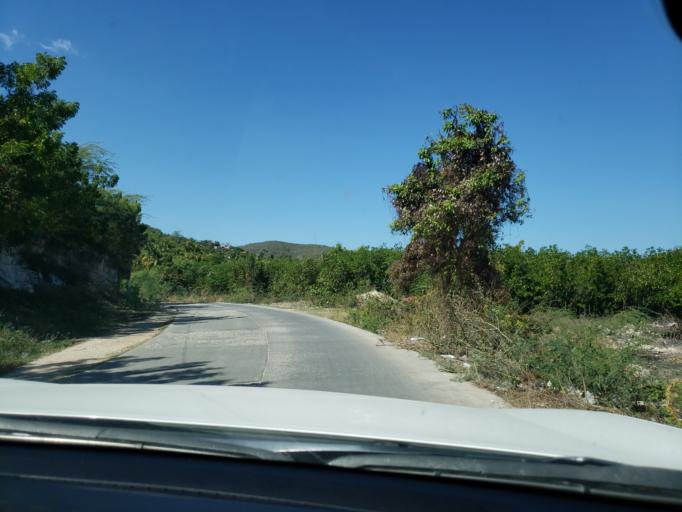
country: HT
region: Nippes
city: Miragoane
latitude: 18.4451
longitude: -73.1025
